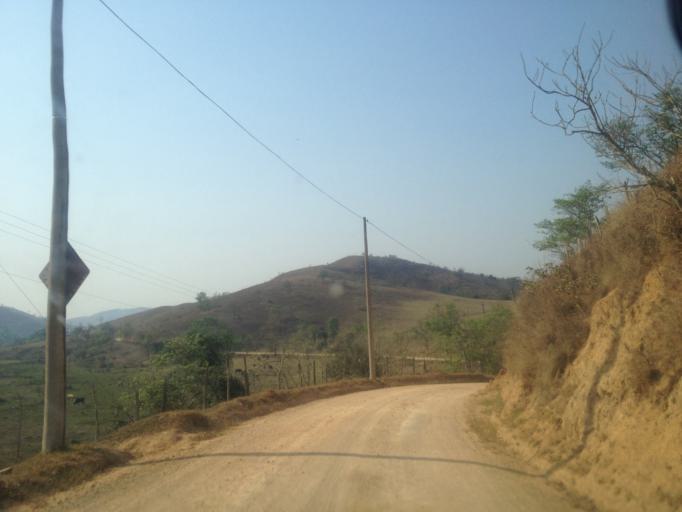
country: BR
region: Rio de Janeiro
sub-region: Resende
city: Resende
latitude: -22.4925
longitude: -44.3558
